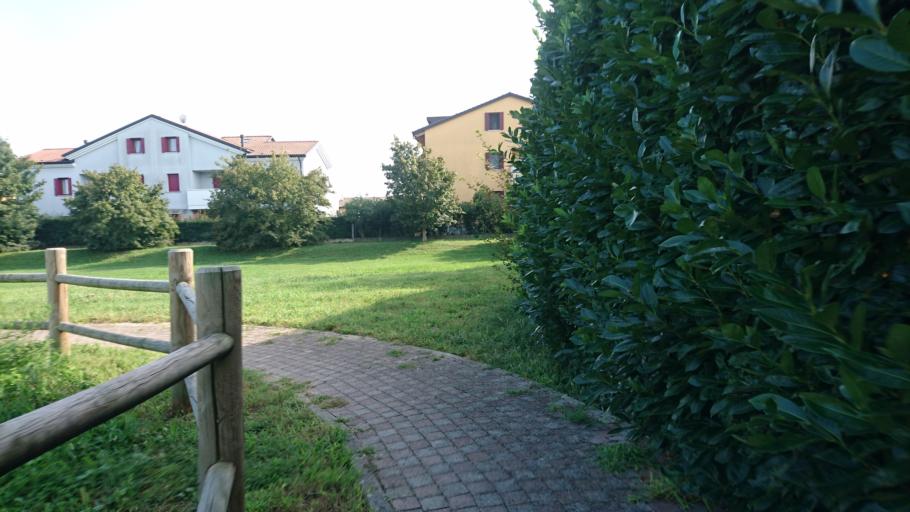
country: IT
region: Veneto
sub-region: Provincia di Padova
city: Tencarola
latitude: 45.3977
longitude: 11.7987
